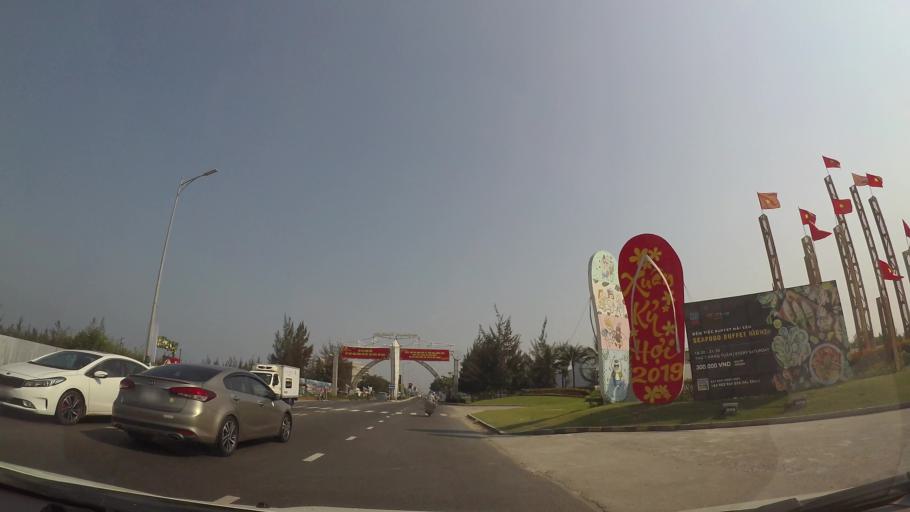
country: VN
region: Da Nang
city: Ngu Hanh Son
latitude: 15.9664
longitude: 108.2852
